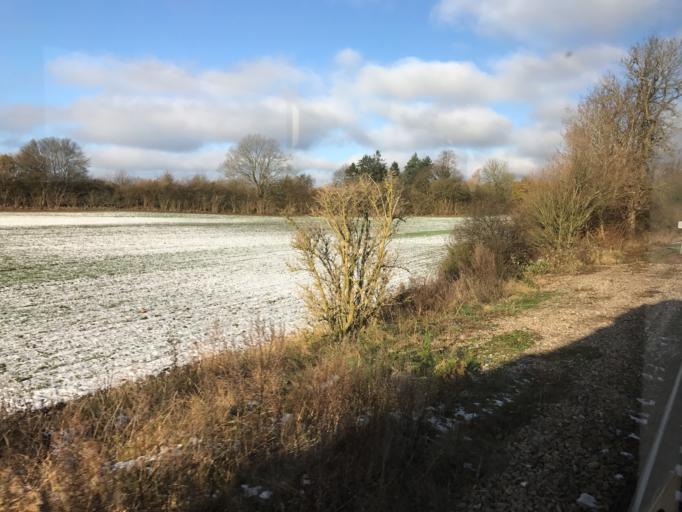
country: DK
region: Zealand
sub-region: Stevns Kommune
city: Stroby Egede
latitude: 55.3989
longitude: 12.1922
